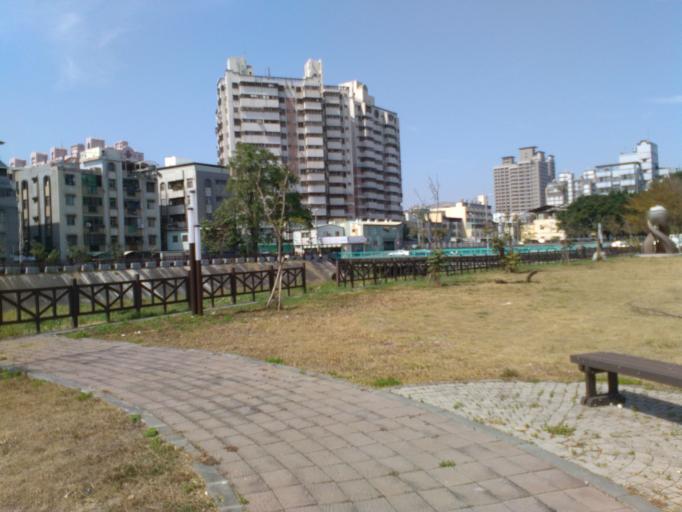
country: TW
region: Taiwan
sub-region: Taichung City
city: Taichung
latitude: 24.1140
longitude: 120.6714
